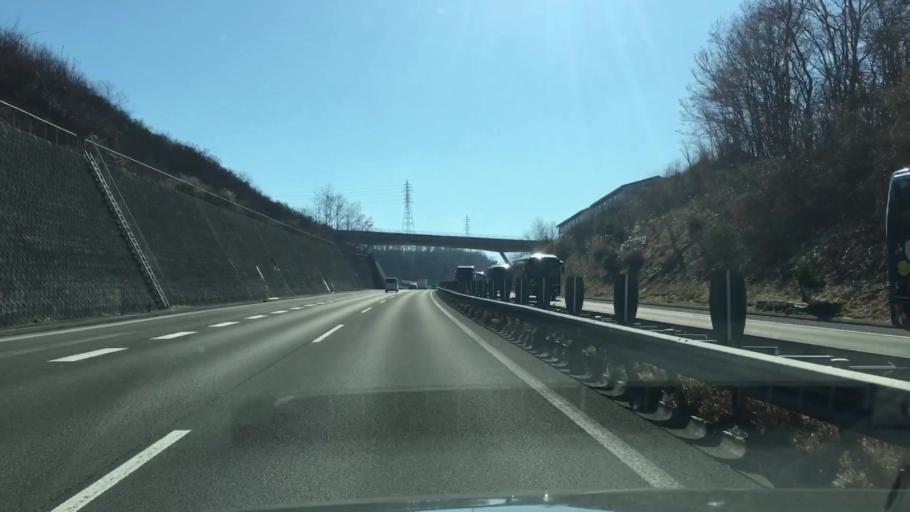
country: JP
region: Nagano
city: Ueda
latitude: 36.4023
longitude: 138.3116
